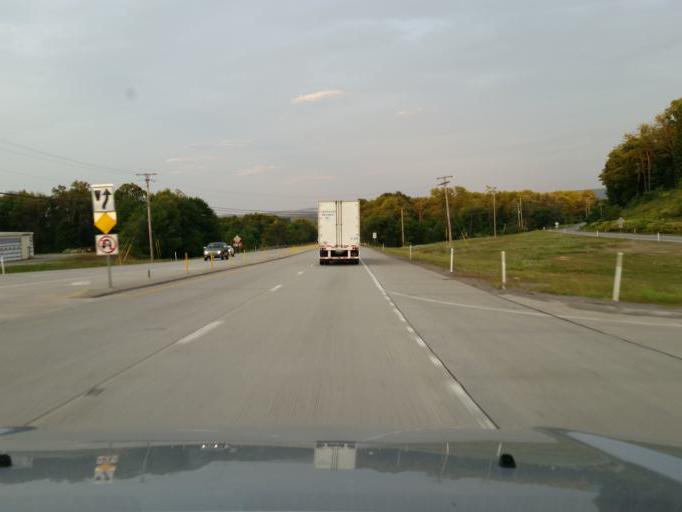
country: US
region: Pennsylvania
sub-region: Indiana County
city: Homer City
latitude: 40.4507
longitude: -79.0584
